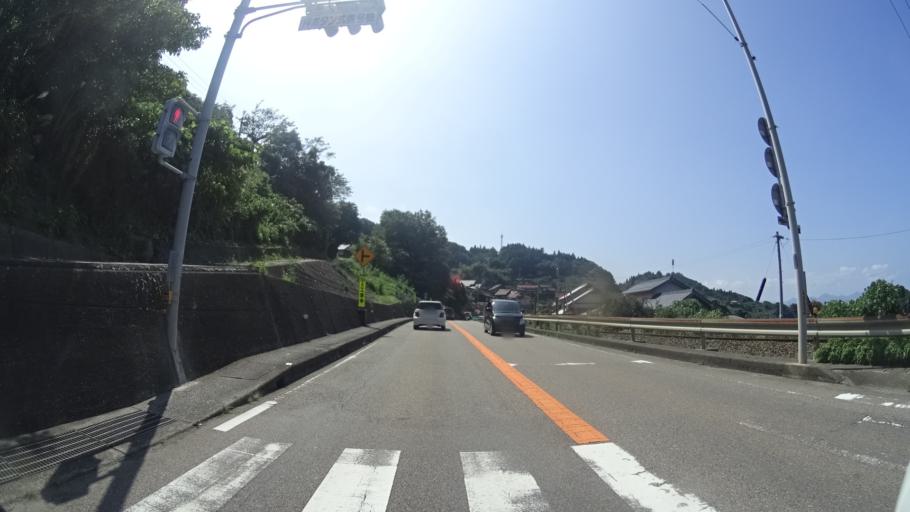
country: JP
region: Shimane
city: Masuda
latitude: 34.7431
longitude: 131.8759
